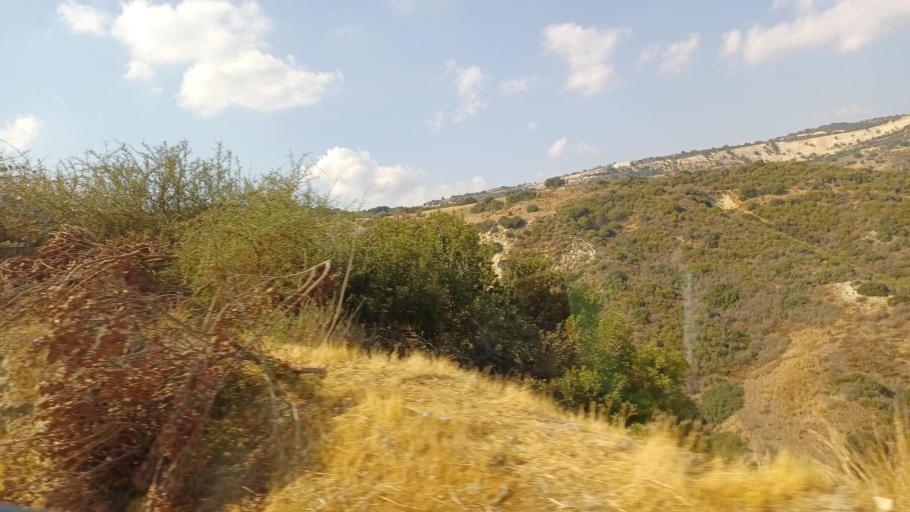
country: CY
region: Pafos
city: Polis
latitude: 34.9945
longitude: 32.4324
